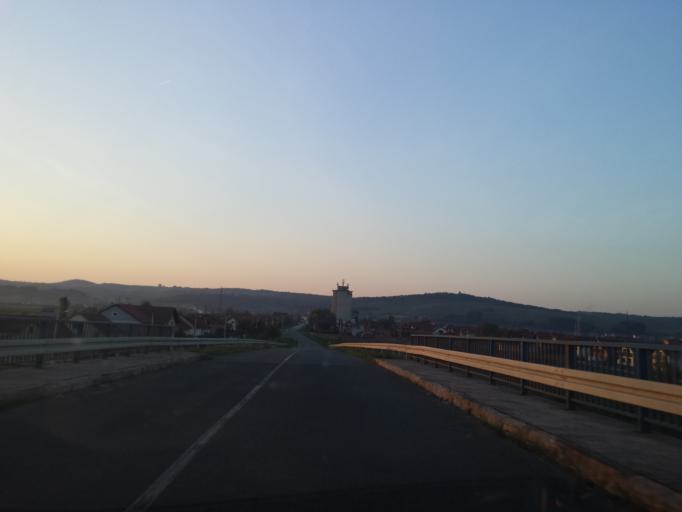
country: HR
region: Brodsko-Posavska
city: Oriovac
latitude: 45.1563
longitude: 17.8158
